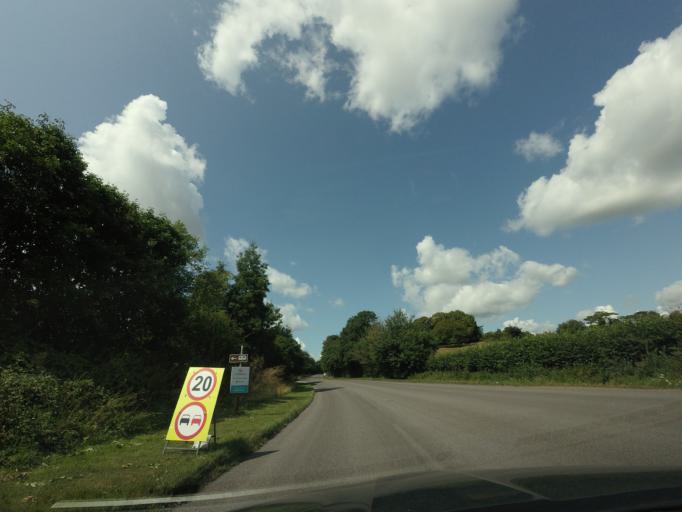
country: GB
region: England
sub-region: Kent
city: Harrietsham
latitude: 51.2644
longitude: 0.6043
